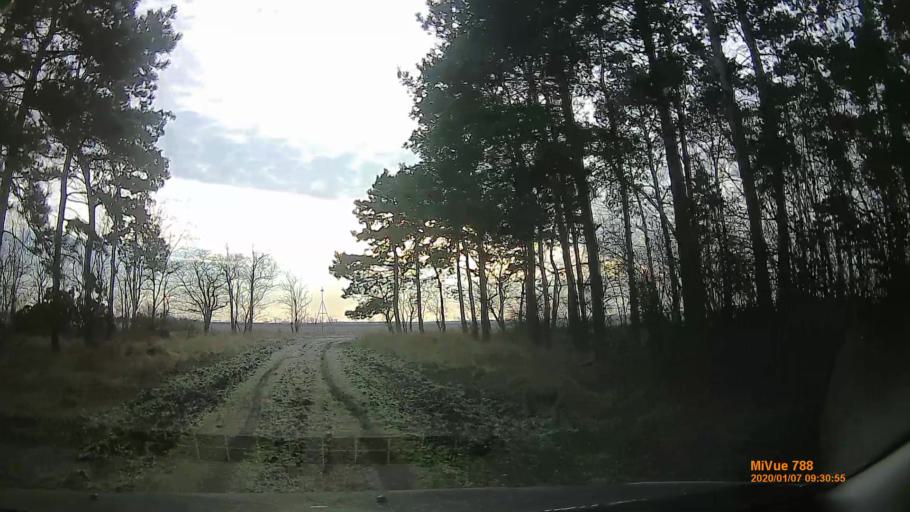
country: HU
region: Gyor-Moson-Sopron
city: Rajka
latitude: 47.9468
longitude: 17.1733
